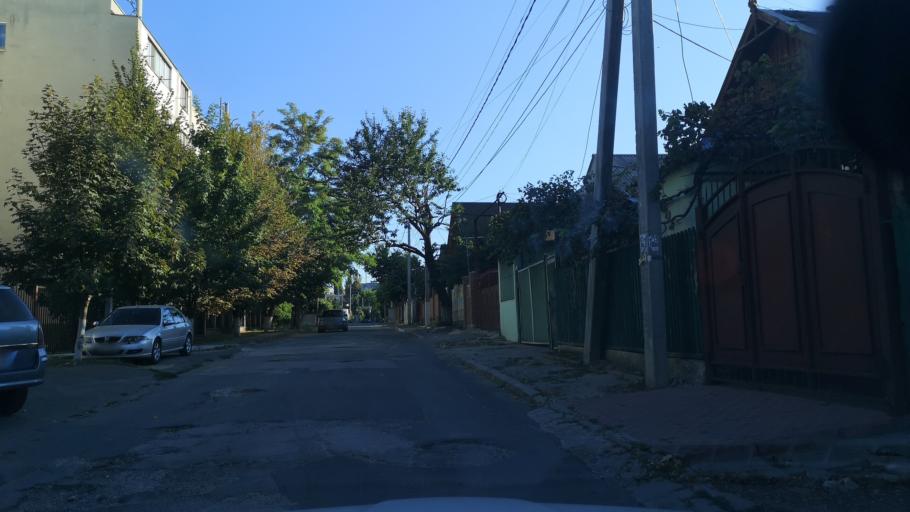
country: MD
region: Chisinau
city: Chisinau
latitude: 46.9892
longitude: 28.8807
